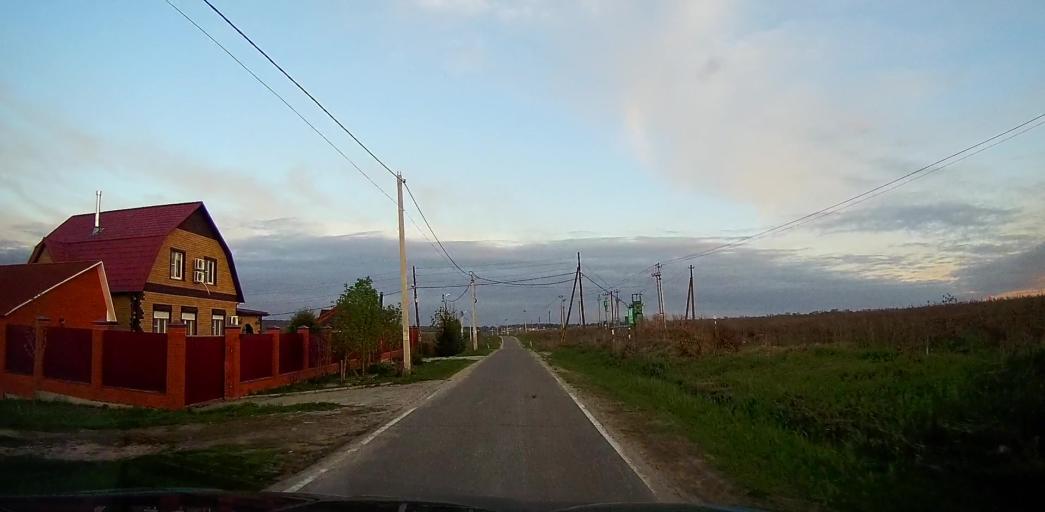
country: RU
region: Moskovskaya
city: Peski
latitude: 55.2286
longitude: 38.7338
